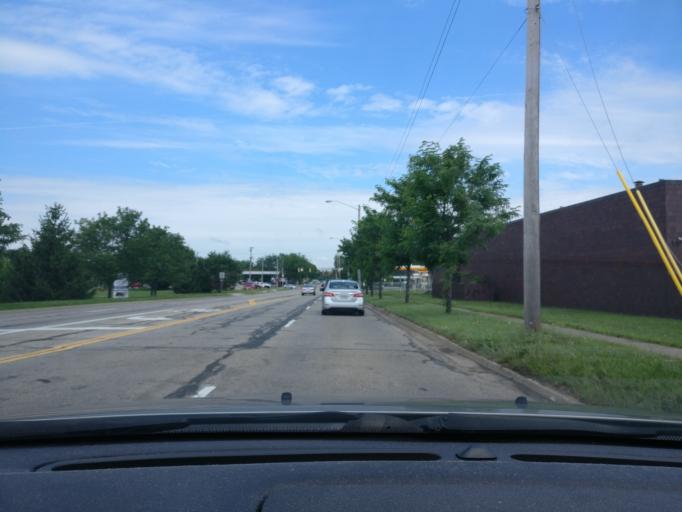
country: US
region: Ohio
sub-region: Montgomery County
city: West Carrollton City
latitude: 39.6741
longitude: -84.2410
